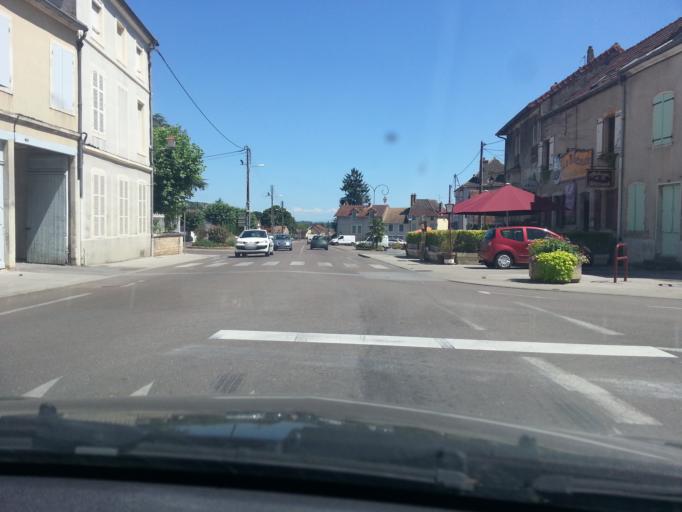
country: FR
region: Bourgogne
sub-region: Departement de Saone-et-Loire
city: Givry
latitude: 46.7820
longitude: 4.7463
